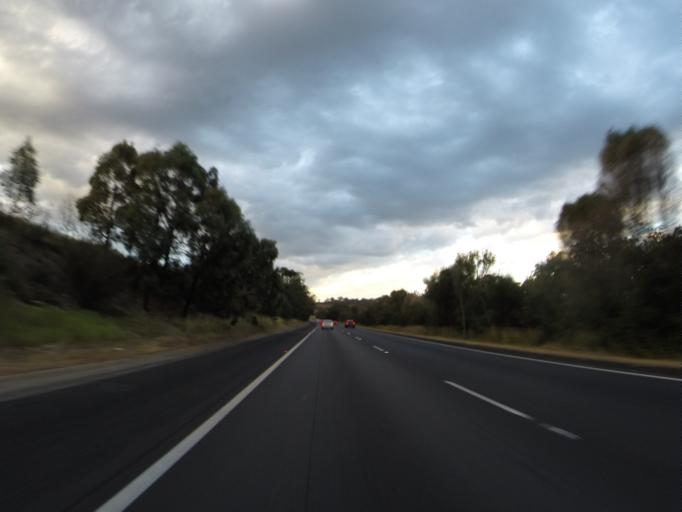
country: AU
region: New South Wales
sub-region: Campbelltown Municipality
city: Glen Alpine
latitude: -34.1224
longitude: 150.7542
